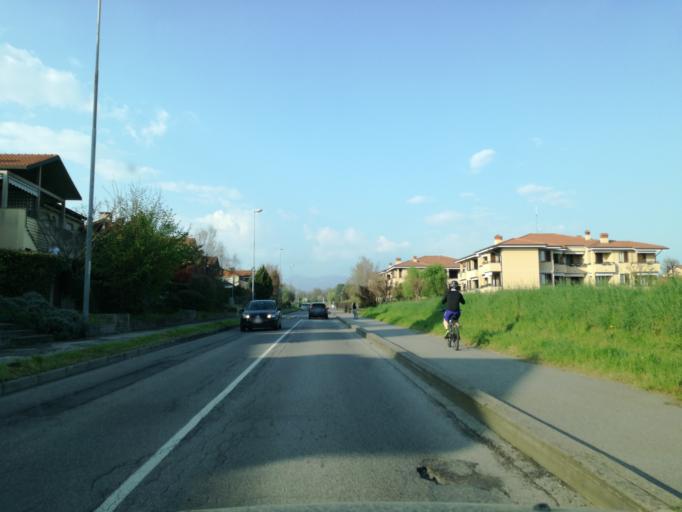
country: IT
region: Lombardy
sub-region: Provincia di Monza e Brianza
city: Carnate
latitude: 45.6527
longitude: 9.3824
